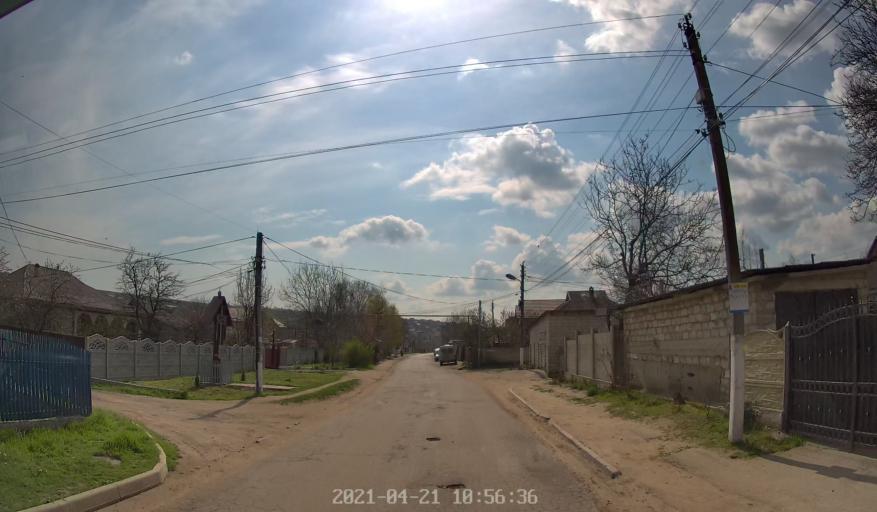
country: MD
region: Chisinau
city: Singera
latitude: 46.9640
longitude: 28.9352
